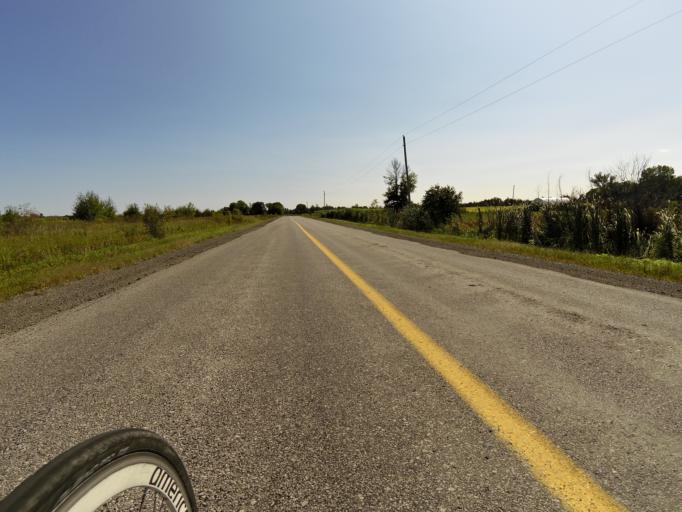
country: CA
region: Ontario
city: Arnprior
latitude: 45.4465
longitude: -76.0789
